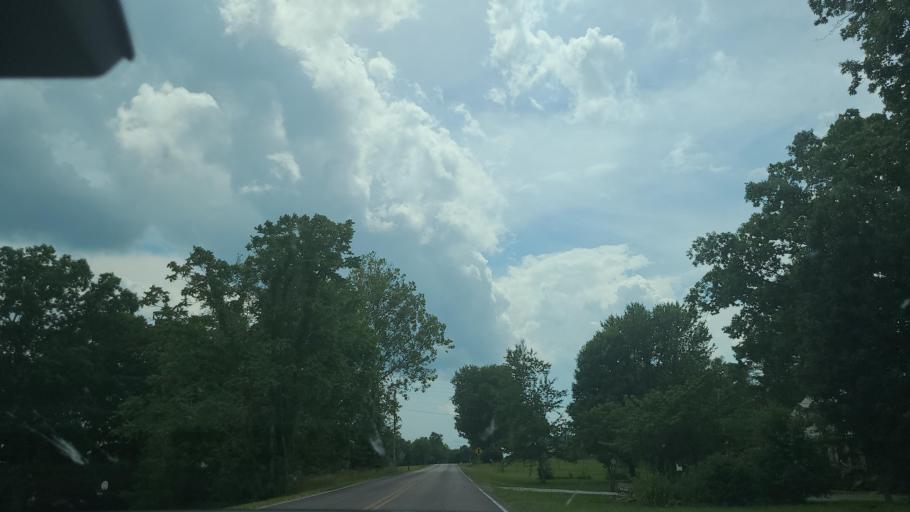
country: US
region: Tennessee
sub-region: Cumberland County
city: Lake Tansi
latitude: 35.8054
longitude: -85.0331
